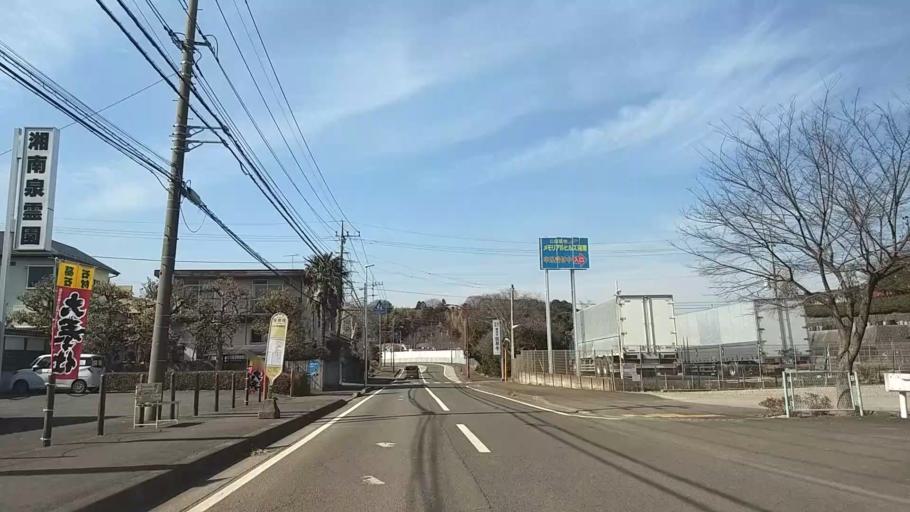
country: JP
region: Kanagawa
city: Fujisawa
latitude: 35.3829
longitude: 139.4331
